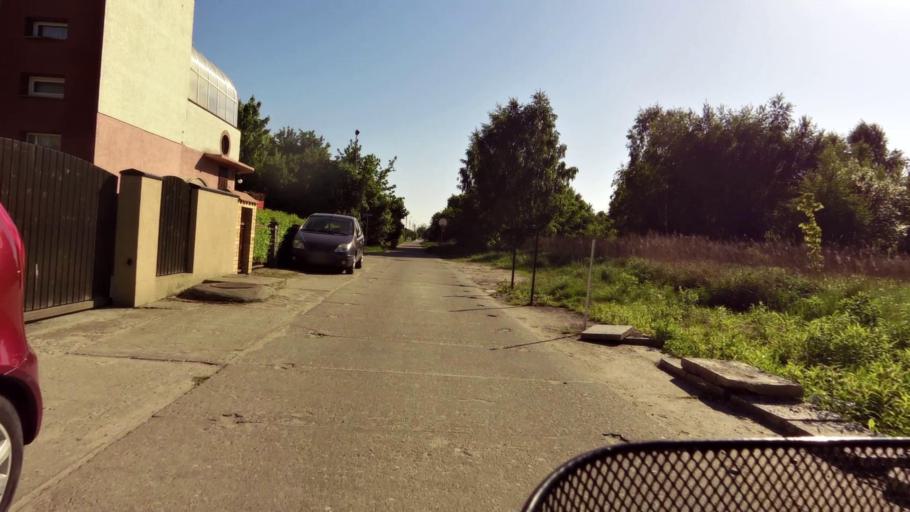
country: PL
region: West Pomeranian Voivodeship
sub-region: Koszalin
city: Koszalin
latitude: 54.1889
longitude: 16.2231
